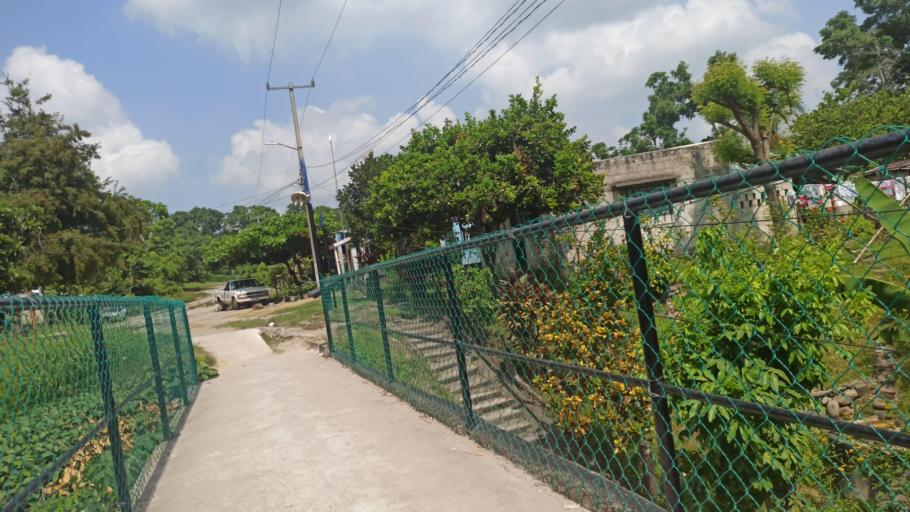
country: MX
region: Puebla
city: San Jose Acateno
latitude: 20.1738
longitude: -97.1100
